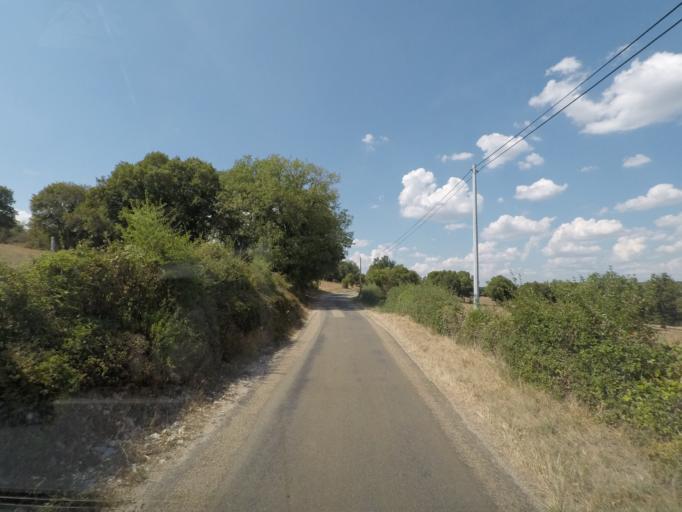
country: FR
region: Midi-Pyrenees
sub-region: Departement du Lot
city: Lalbenque
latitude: 44.5188
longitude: 1.6287
